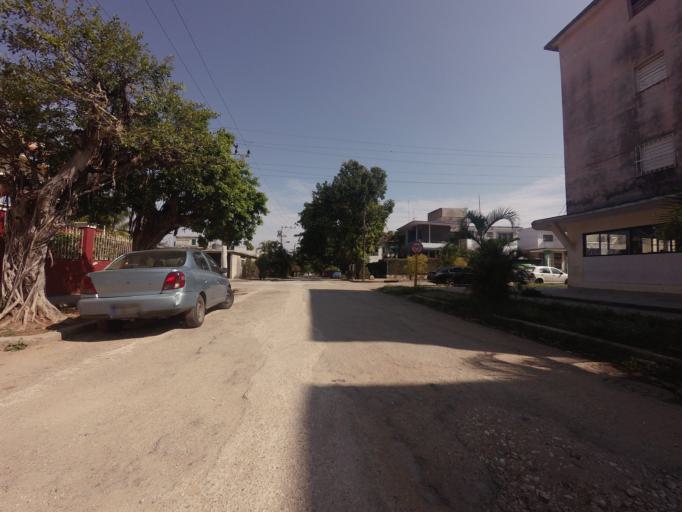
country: CU
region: La Habana
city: Havana
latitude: 23.1147
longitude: -82.4202
